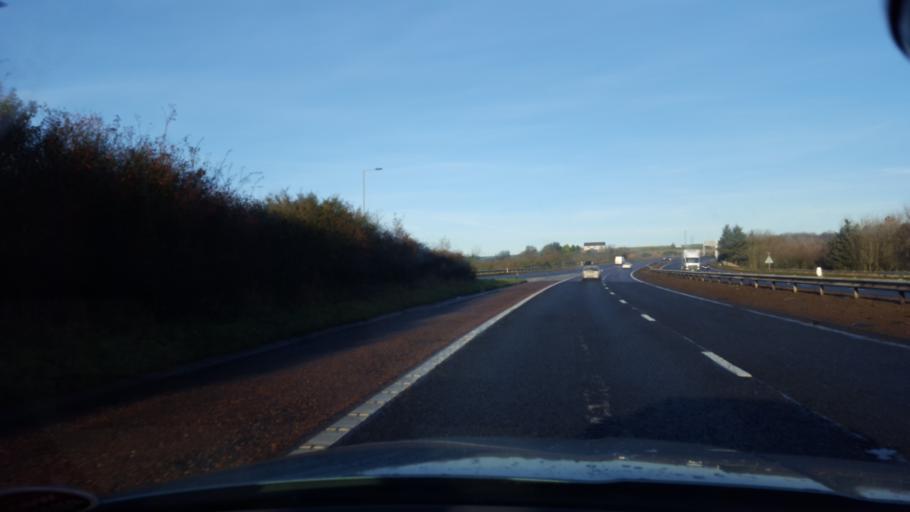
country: GB
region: Scotland
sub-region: Fife
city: Crossgates
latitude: 56.0829
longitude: -3.3996
